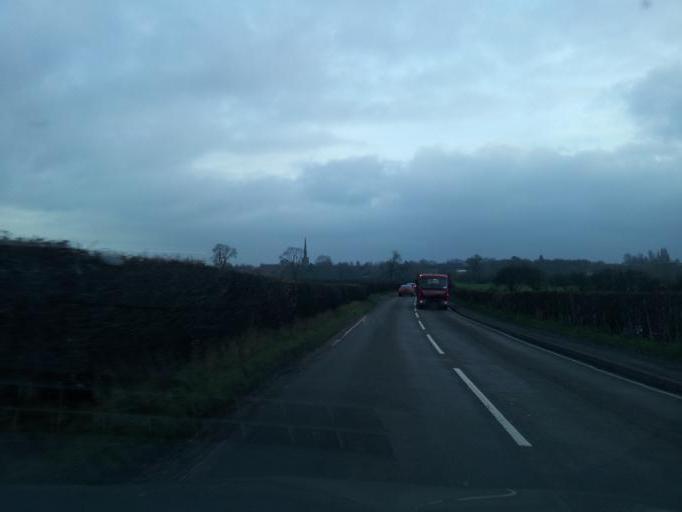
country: GB
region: England
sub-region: Derbyshire
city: Repton
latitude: 52.8475
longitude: -1.5609
